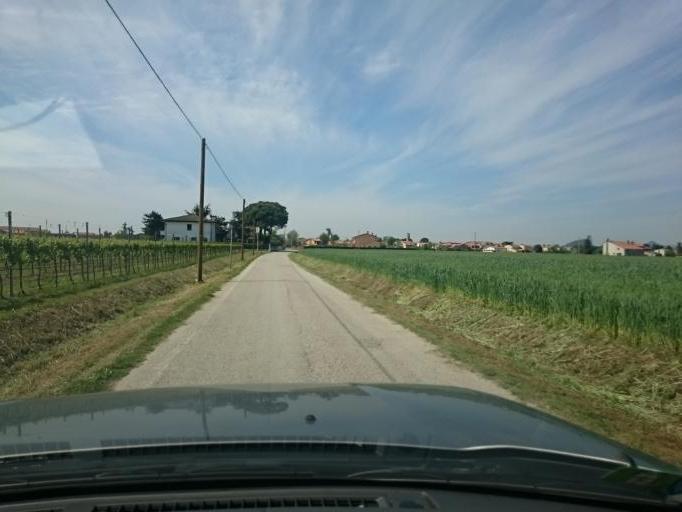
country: IT
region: Veneto
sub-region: Provincia di Padova
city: San Pietro Viminario
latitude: 45.2490
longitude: 11.8292
